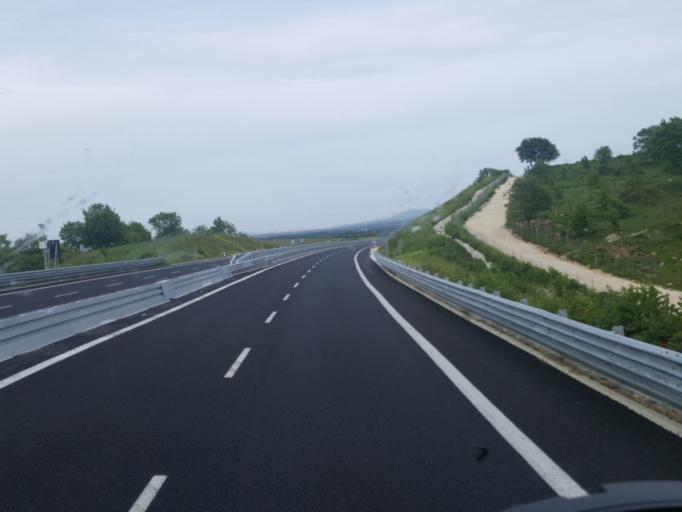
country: IT
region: Latium
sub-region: Provincia di Viterbo
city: Monte Romano
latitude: 42.2931
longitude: 11.9425
